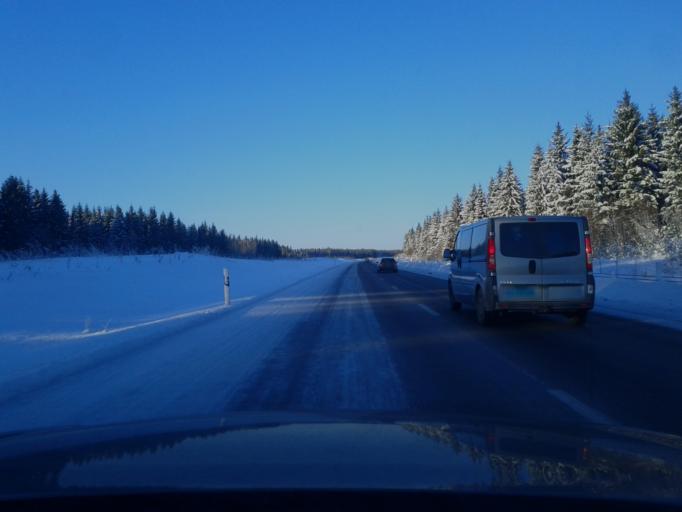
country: SE
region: Uppsala
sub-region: Tierps Kommun
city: Tierp
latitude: 60.4162
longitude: 17.4522
